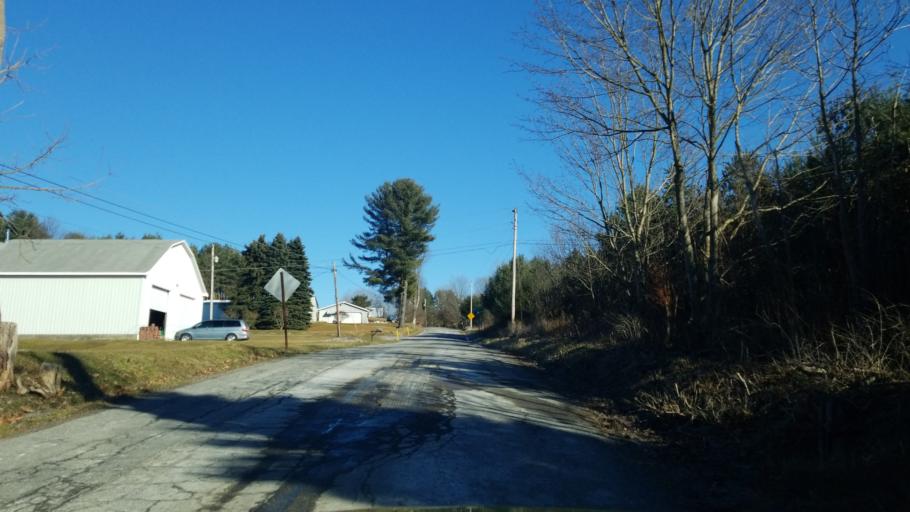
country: US
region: Pennsylvania
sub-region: Clearfield County
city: Sandy
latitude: 41.0478
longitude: -78.7582
